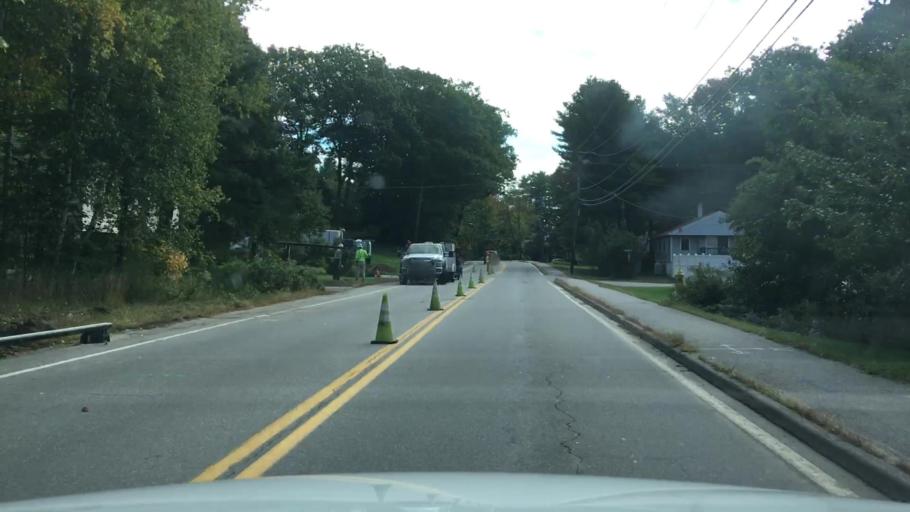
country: US
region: Maine
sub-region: Cumberland County
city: Brunswick
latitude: 43.9244
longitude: -69.9468
